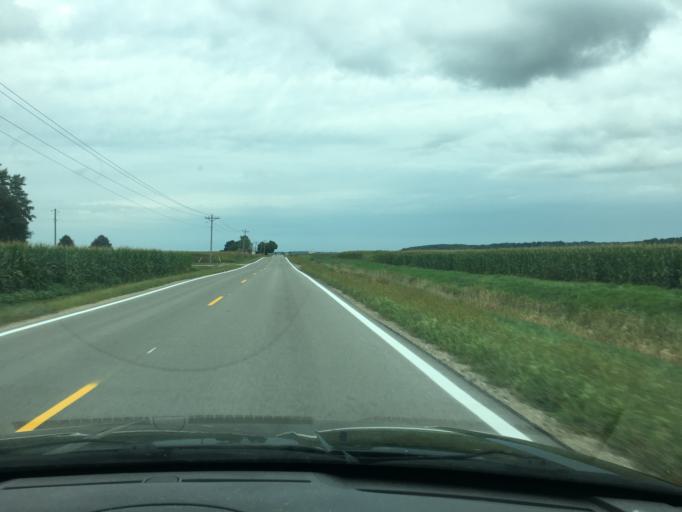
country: US
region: Ohio
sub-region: Champaign County
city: Urbana
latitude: 40.1653
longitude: -83.7838
